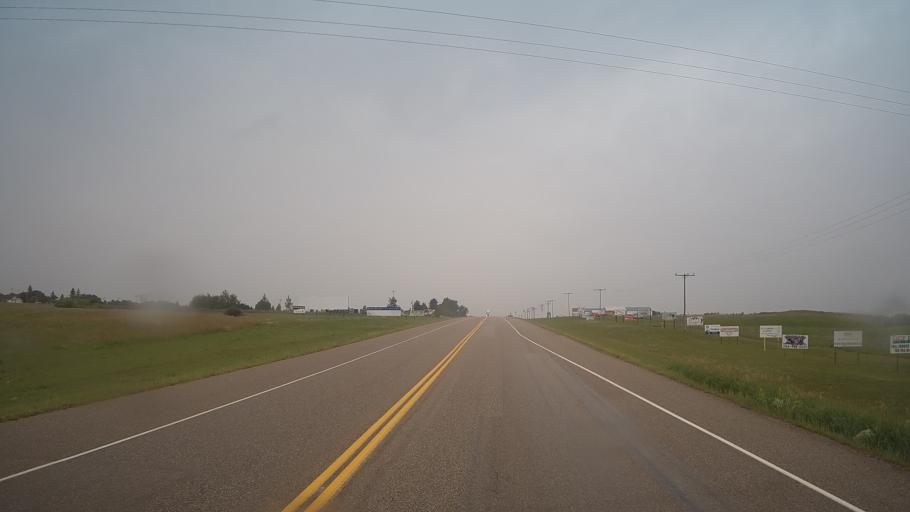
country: CA
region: Saskatchewan
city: Biggar
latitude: 52.0598
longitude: -107.9667
